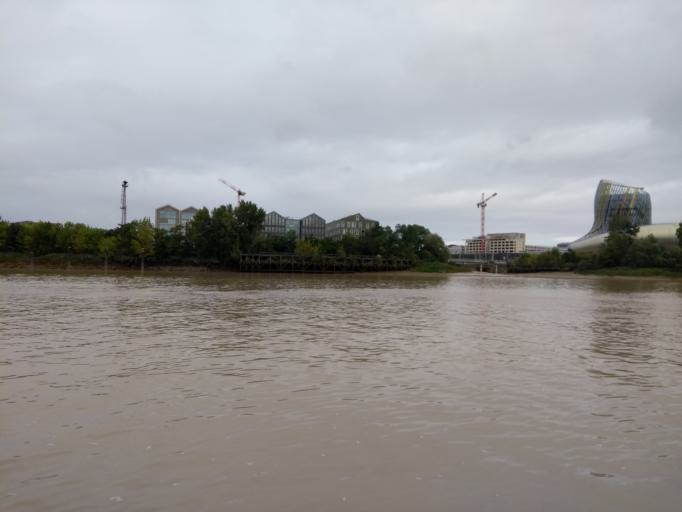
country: FR
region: Aquitaine
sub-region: Departement de la Gironde
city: Cenon
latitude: 44.8590
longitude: -0.5503
